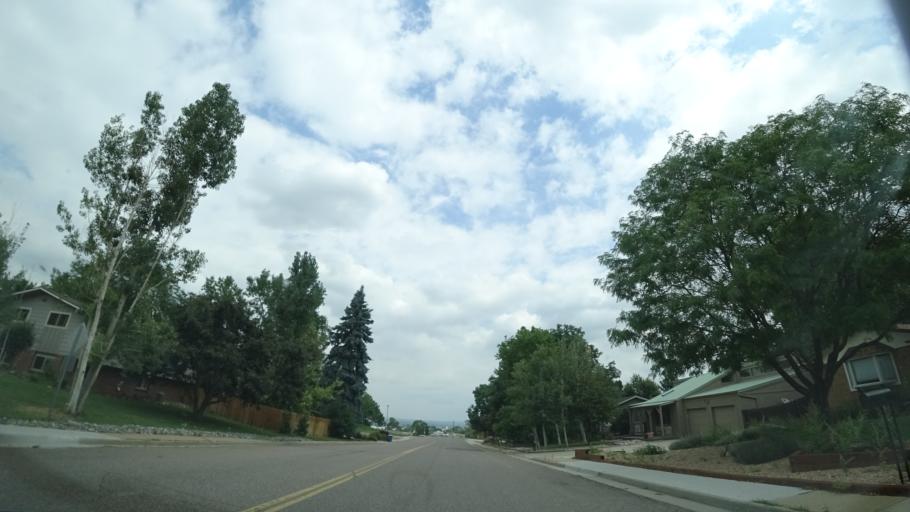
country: US
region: Colorado
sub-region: Jefferson County
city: West Pleasant View
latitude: 39.7226
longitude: -105.1597
